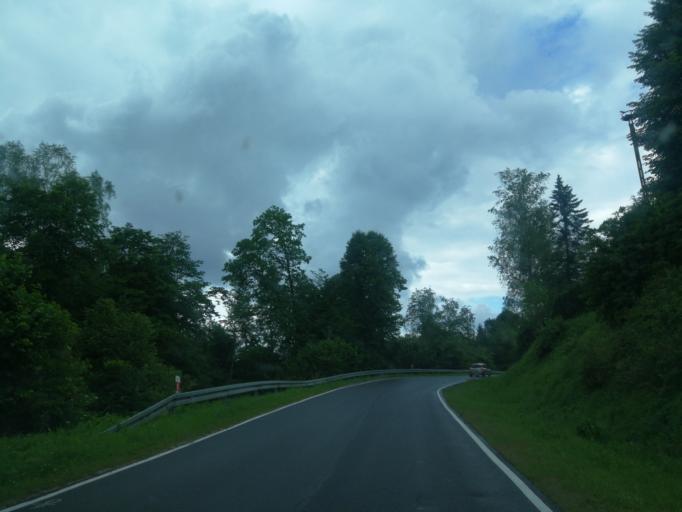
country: PL
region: Subcarpathian Voivodeship
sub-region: Powiat leski
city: Olszanica
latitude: 49.4328
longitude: 22.4557
